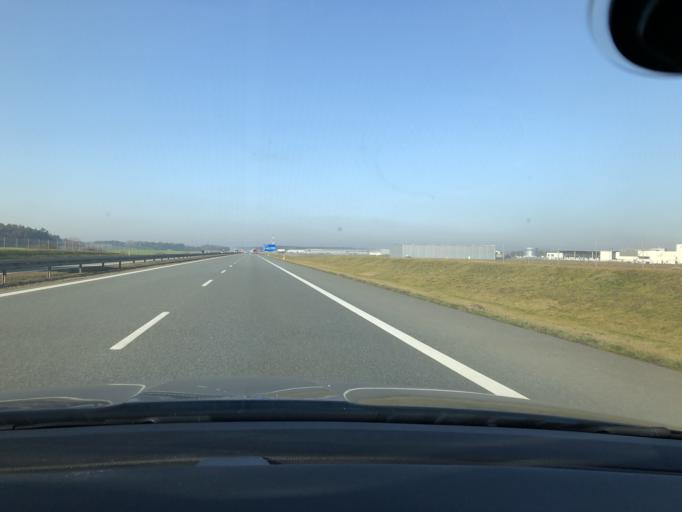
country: PL
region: Greater Poland Voivodeship
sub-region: Powiat poznanski
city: Buk
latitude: 52.3662
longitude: 16.5950
